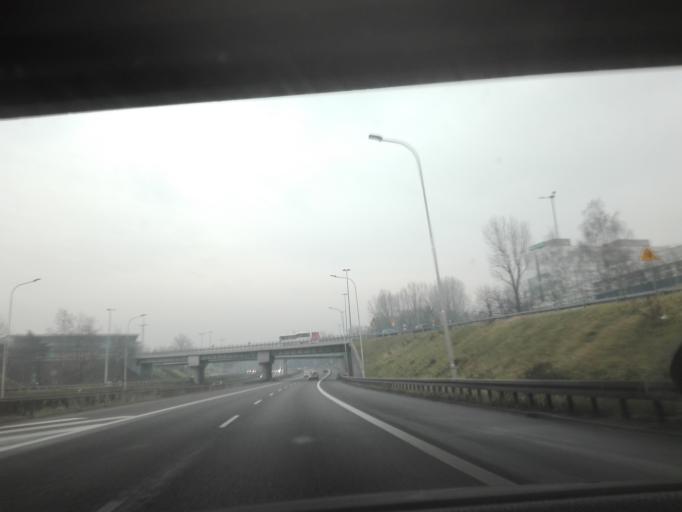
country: PL
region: Silesian Voivodeship
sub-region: Katowice
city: Katowice
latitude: 50.2497
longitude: 18.9999
